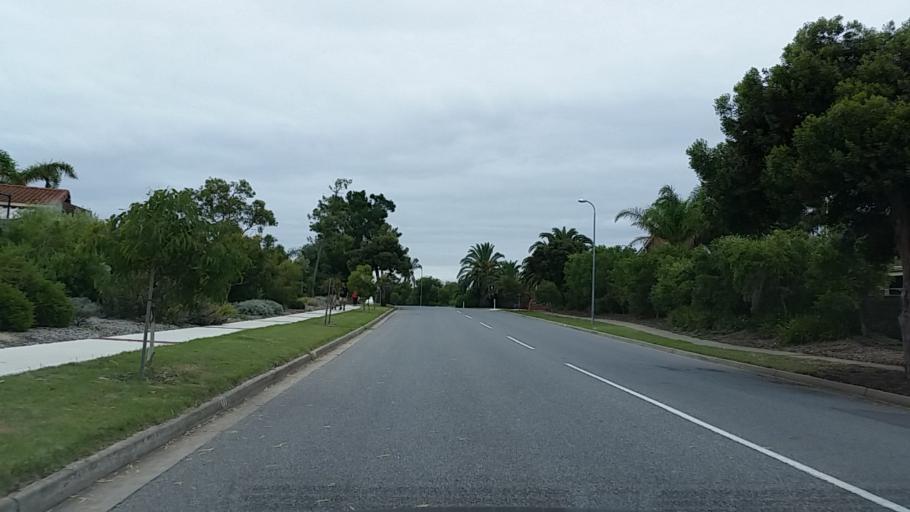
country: AU
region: South Australia
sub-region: Charles Sturt
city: West Lakes Shore
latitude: -34.8623
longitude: 138.4964
